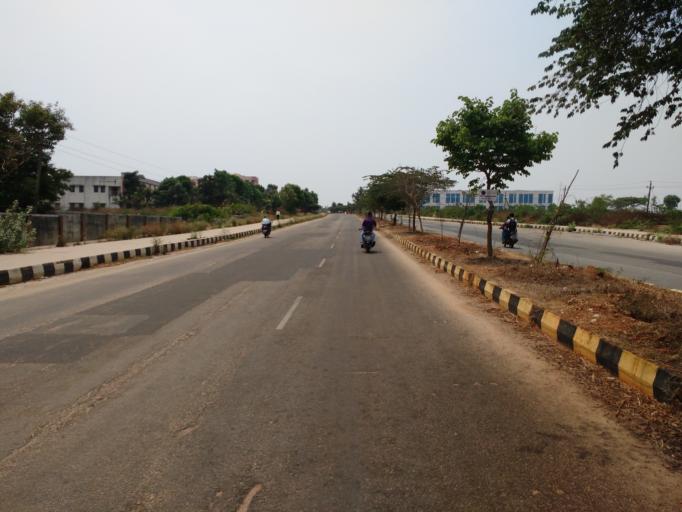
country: IN
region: Karnataka
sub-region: Hassan
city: Hassan
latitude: 13.0139
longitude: 76.1192
